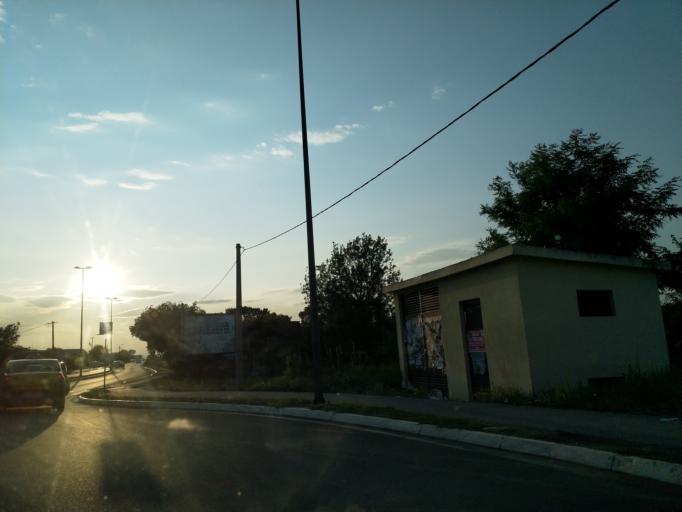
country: RS
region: Central Serbia
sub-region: Raski Okrug
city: Vrnjacka Banja
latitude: 43.6401
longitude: 20.9209
